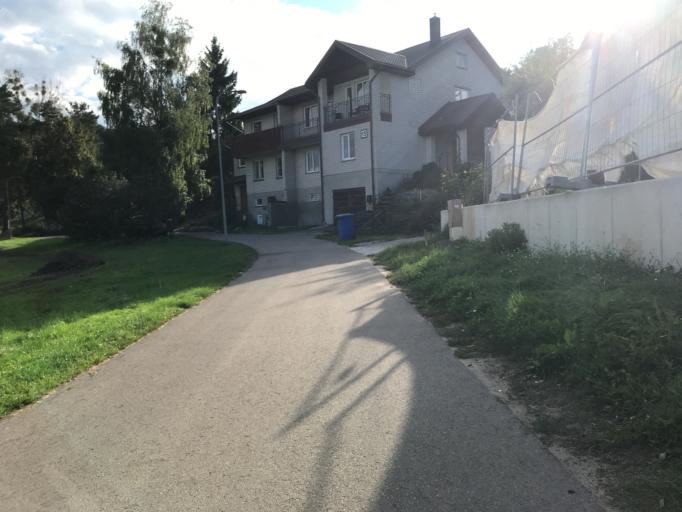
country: LT
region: Alytaus apskritis
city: Druskininkai
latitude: 54.0180
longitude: 23.9598
